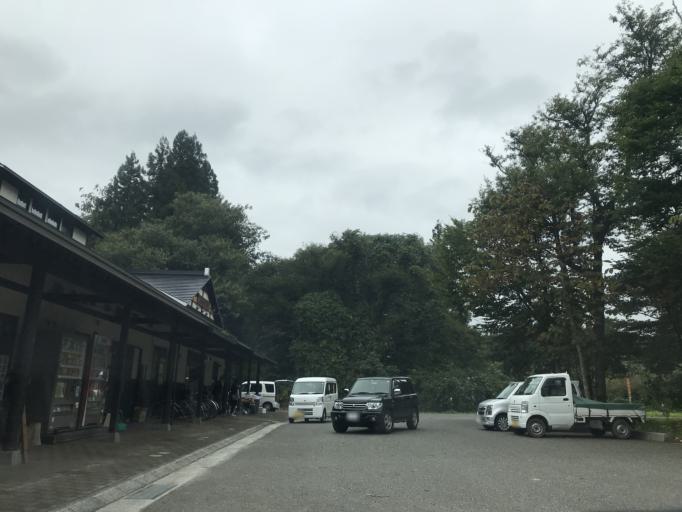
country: JP
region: Iwate
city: Ichinoseki
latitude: 38.9723
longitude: 140.9599
